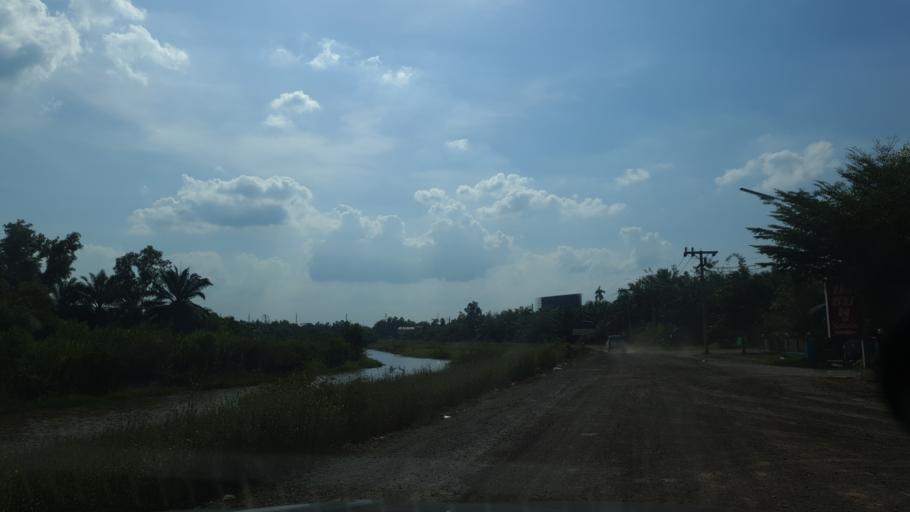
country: TH
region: Surat Thani
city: Phunphin
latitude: 9.1449
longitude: 99.1613
